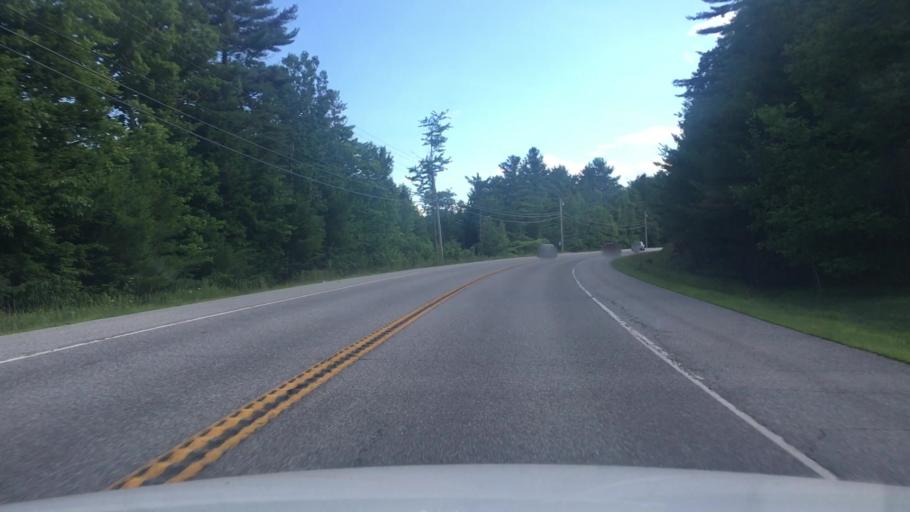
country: US
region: Maine
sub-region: Androscoggin County
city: Livermore Falls
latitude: 44.4498
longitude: -70.1986
